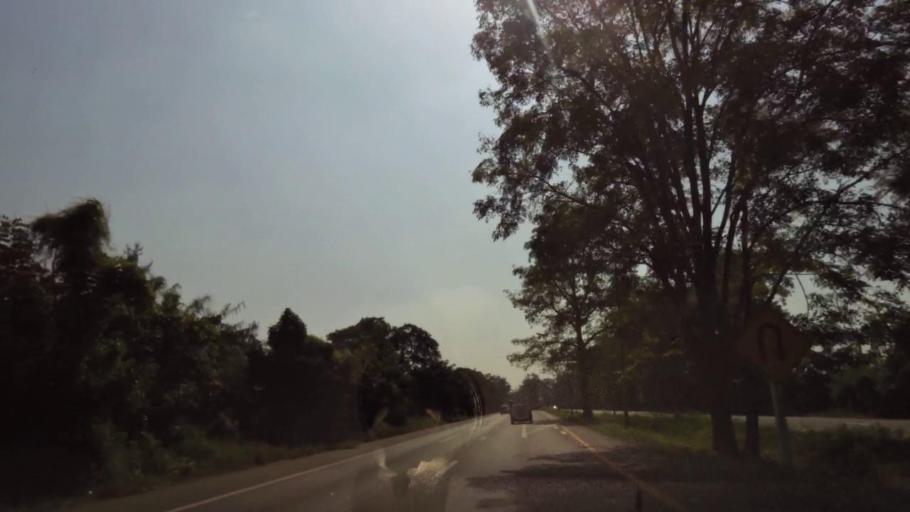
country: TH
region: Phichit
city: Bueng Na Rang
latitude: 16.0366
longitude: 100.1168
